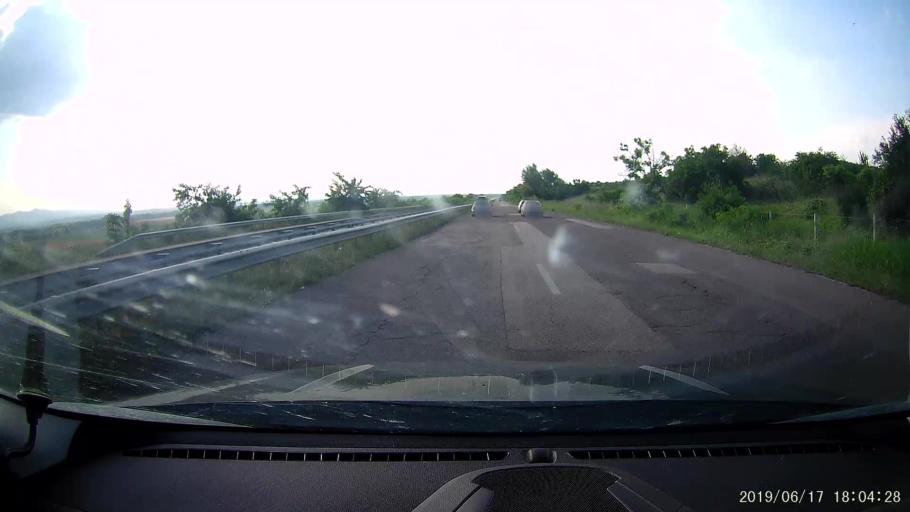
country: BG
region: Khaskovo
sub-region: Obshtina Svilengrad
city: Svilengrad
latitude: 41.7862
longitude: 26.1971
